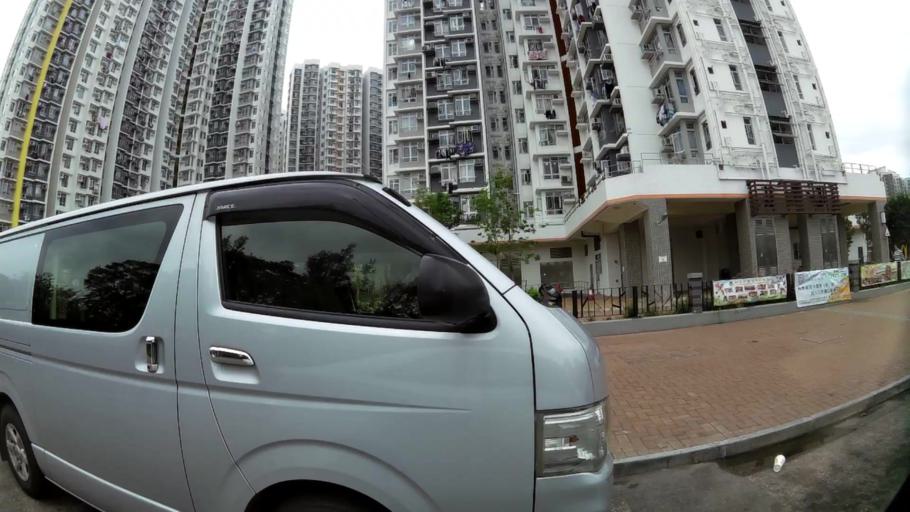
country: HK
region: Yuen Long
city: Yuen Long Kau Hui
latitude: 22.4365
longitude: 113.9971
